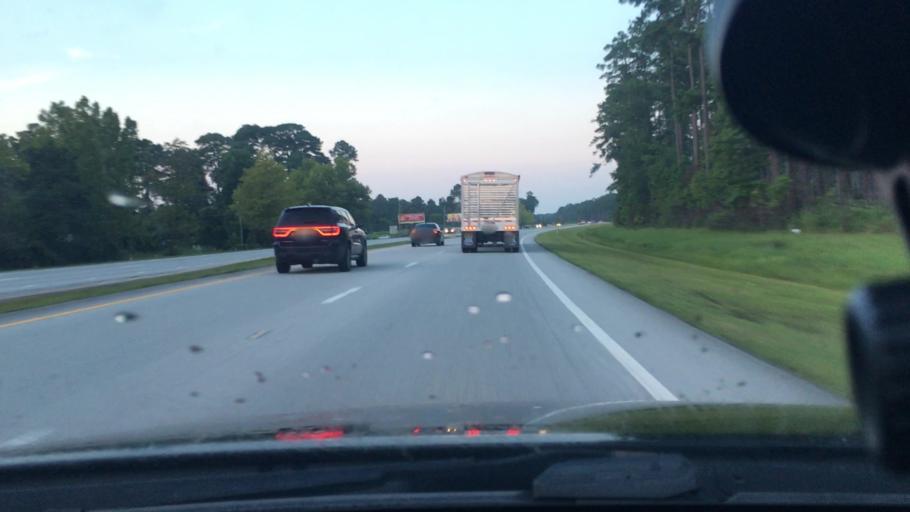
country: US
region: North Carolina
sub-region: Craven County
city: Neuse Forest
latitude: 34.9470
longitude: -76.9485
